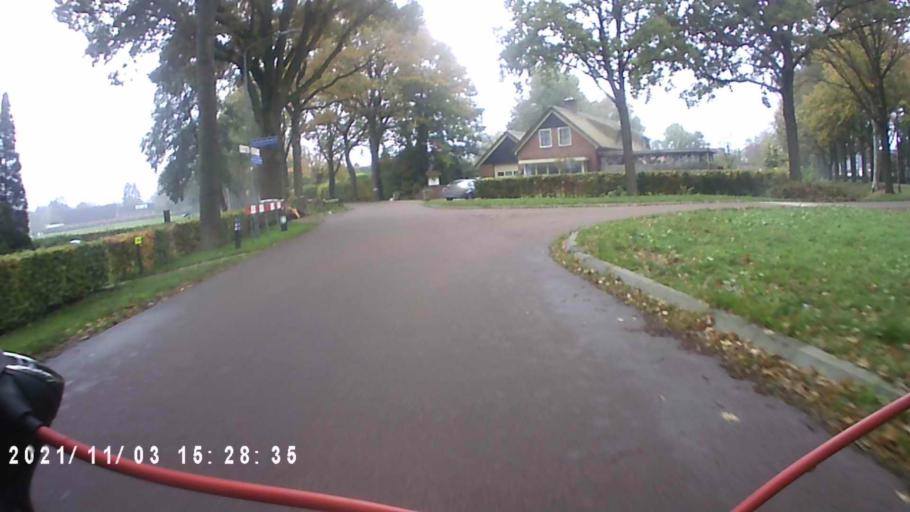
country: NL
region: Groningen
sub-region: Gemeente Leek
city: Leek
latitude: 53.1386
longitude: 6.3747
